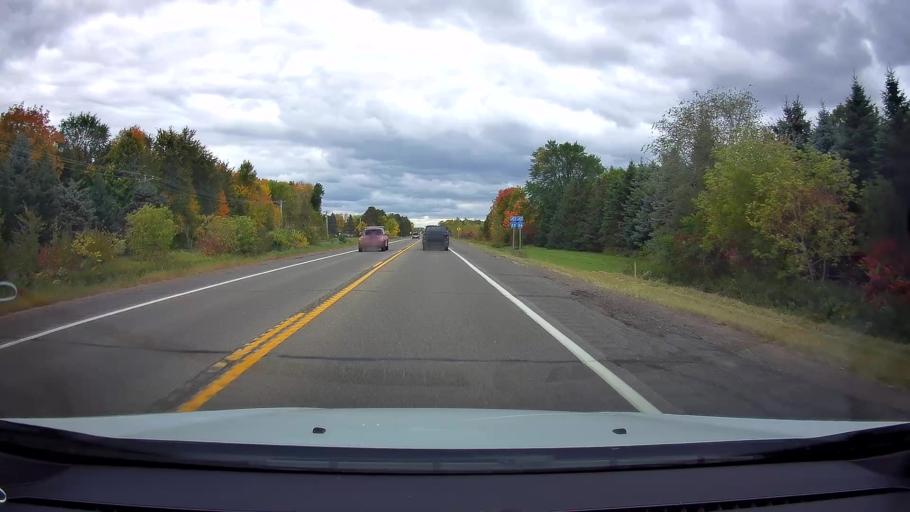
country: US
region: Minnesota
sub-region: Chisago County
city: Chisago City
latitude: 45.3610
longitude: -92.9074
